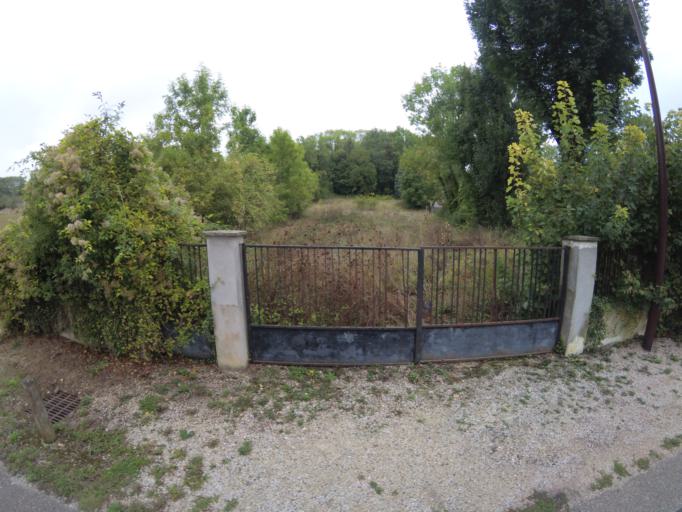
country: FR
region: Ile-de-France
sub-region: Departement de Seine-et-Marne
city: Conches-sur-Gondoire
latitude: 48.8601
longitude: 2.7161
